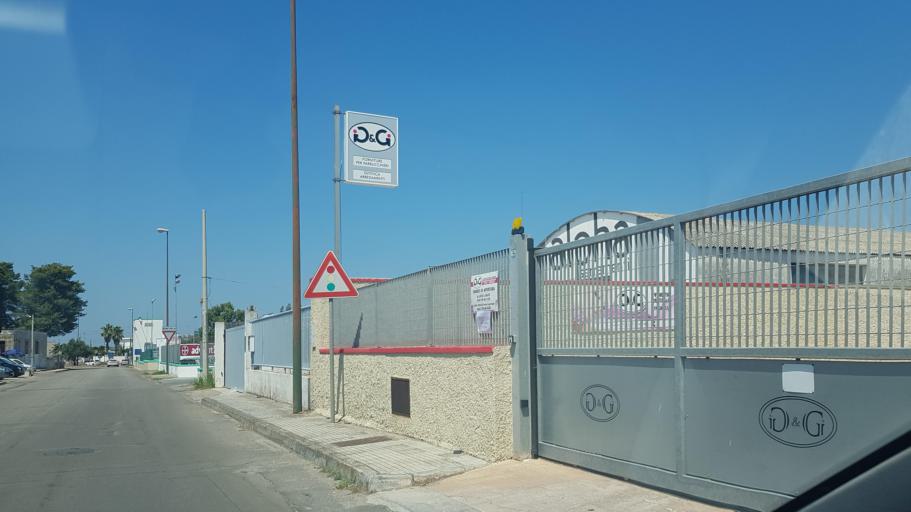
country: IT
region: Apulia
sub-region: Provincia di Lecce
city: Melendugno
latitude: 40.2773
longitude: 18.3442
